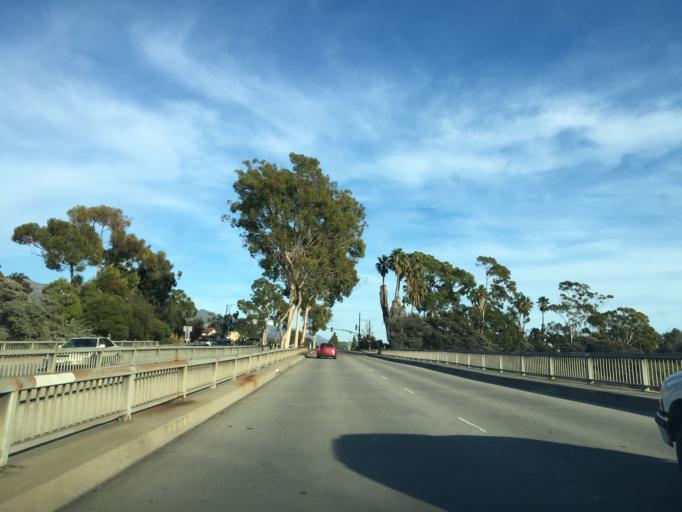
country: US
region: California
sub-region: Santa Barbara County
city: Mission Canyon
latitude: 34.4402
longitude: -119.7562
